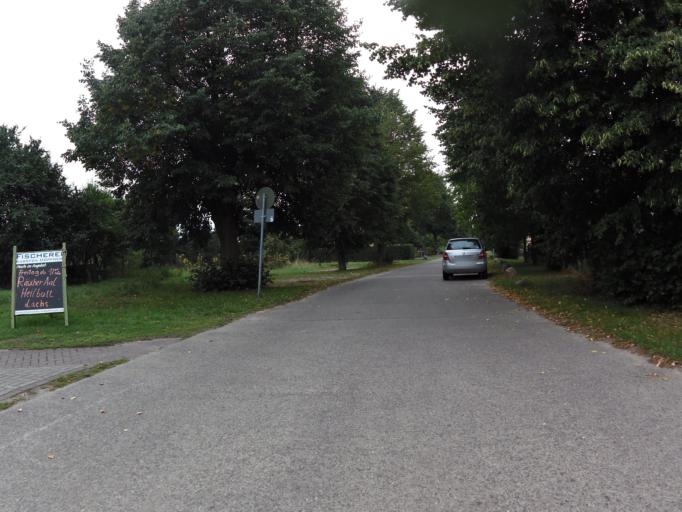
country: DE
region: Mecklenburg-Vorpommern
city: Seebad Heringsdorf
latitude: 53.8812
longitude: 14.1705
